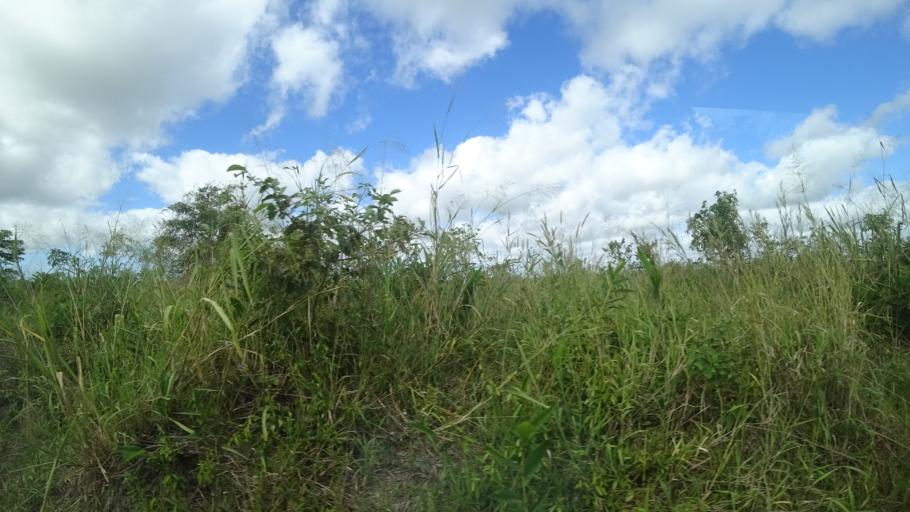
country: MZ
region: Sofala
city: Dondo
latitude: -19.5755
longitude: 35.0925
